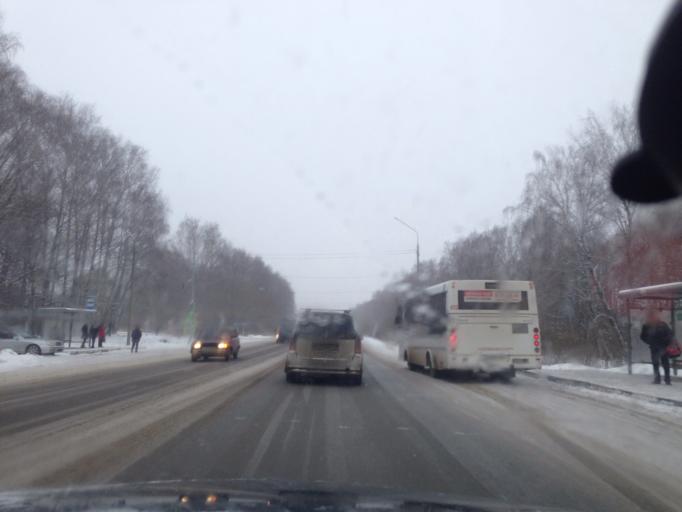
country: RU
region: Tula
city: Skuratovskiy
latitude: 54.1237
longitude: 37.6914
